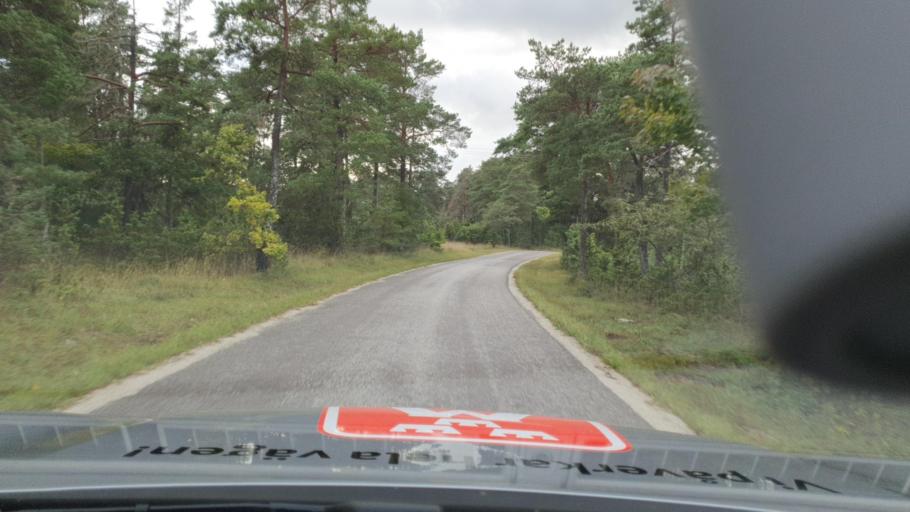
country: SE
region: Gotland
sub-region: Gotland
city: Vibble
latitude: 57.5478
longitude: 18.2376
